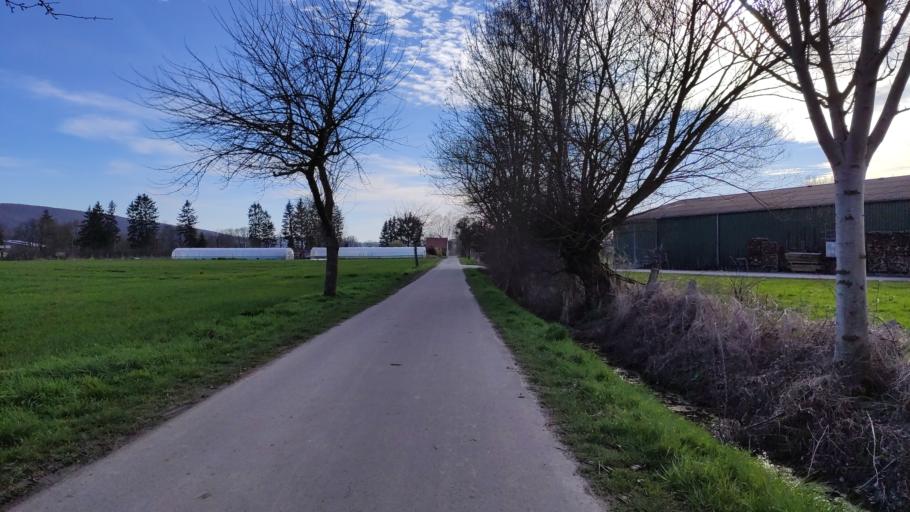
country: DE
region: Lower Saxony
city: Boffzen
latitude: 51.7344
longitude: 9.3676
